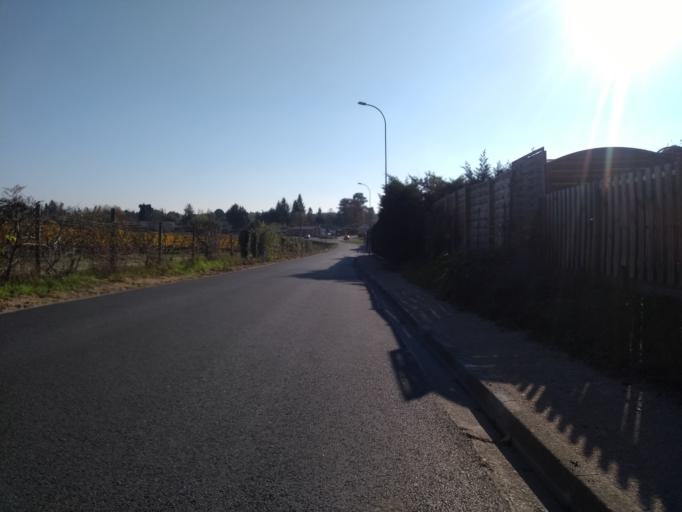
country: FR
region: Aquitaine
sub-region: Departement de la Gironde
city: Leognan
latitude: 44.7258
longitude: -0.5940
